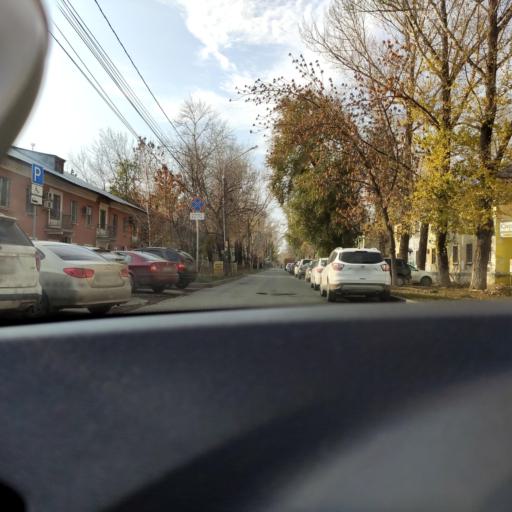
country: RU
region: Samara
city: Samara
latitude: 53.2219
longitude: 50.2590
